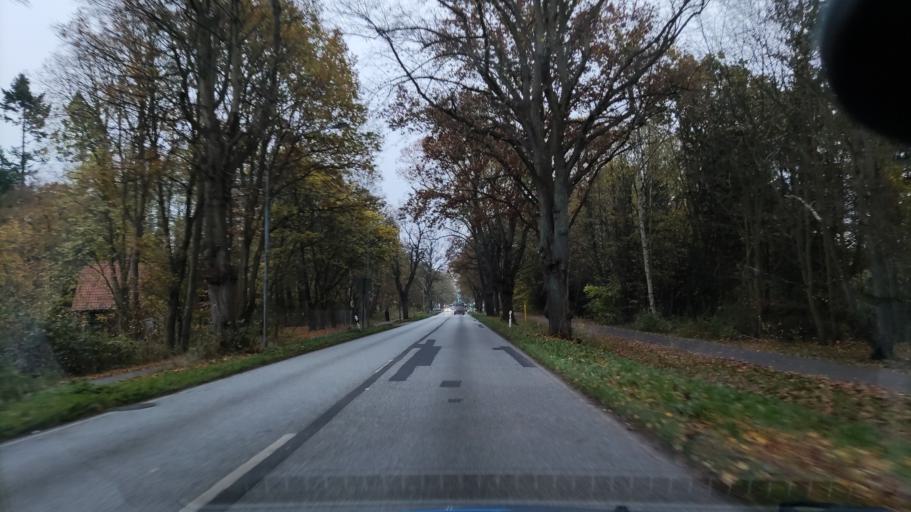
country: DE
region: Schleswig-Holstein
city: Gross Gronau
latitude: 53.8275
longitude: 10.7196
